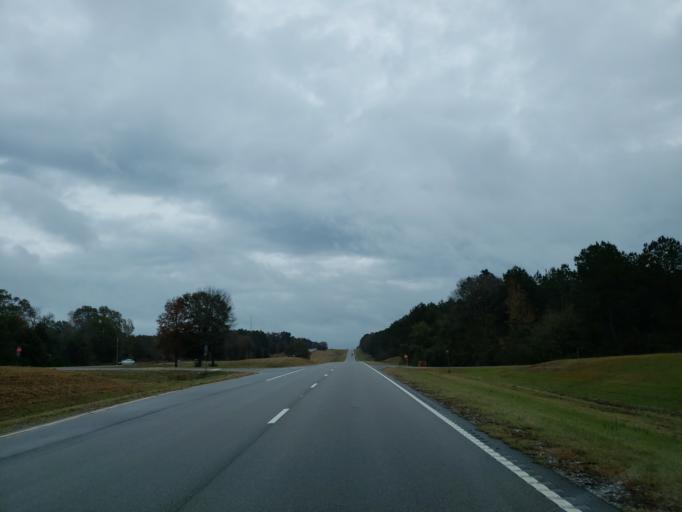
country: US
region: Mississippi
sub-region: Wayne County
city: Waynesboro
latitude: 31.6951
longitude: -88.7587
